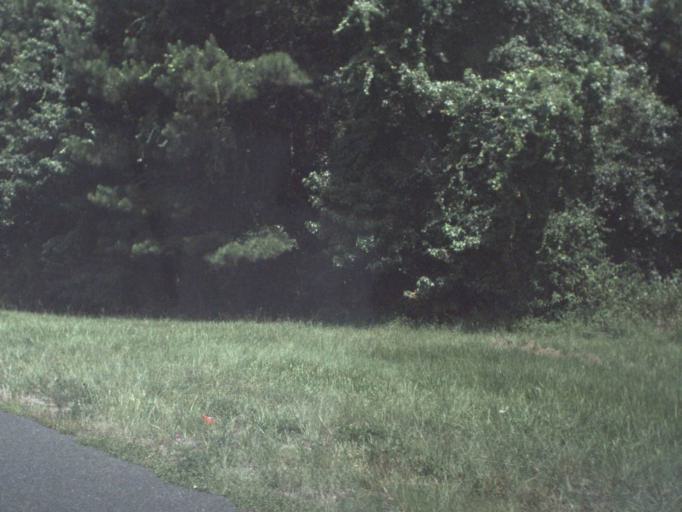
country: US
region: Florida
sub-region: Alachua County
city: Gainesville
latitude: 29.6073
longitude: -82.2280
